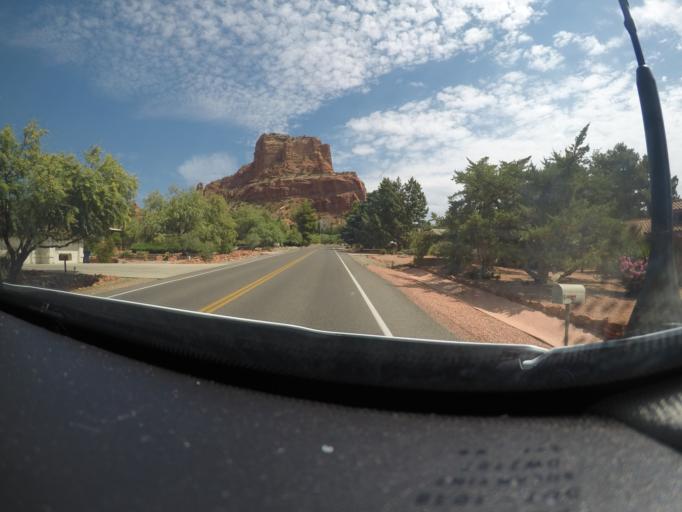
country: US
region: Arizona
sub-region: Yavapai County
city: Big Park
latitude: 34.7854
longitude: -111.7724
